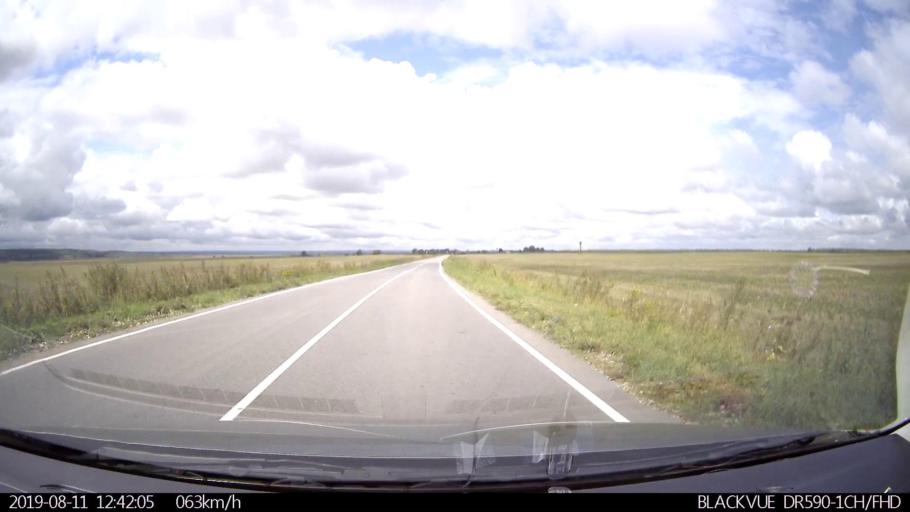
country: RU
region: Ulyanovsk
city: Ignatovka
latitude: 53.8432
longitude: 47.7557
